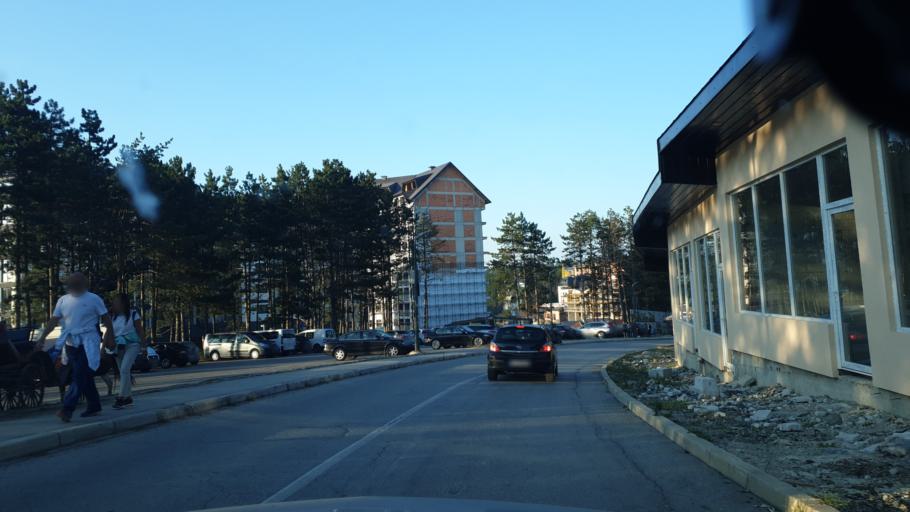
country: RS
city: Zlatibor
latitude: 43.7228
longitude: 19.6955
